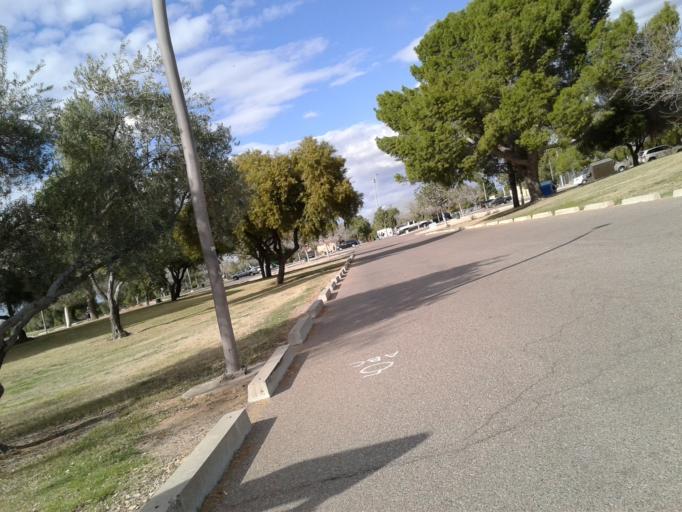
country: US
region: Arizona
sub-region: Maricopa County
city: Paradise Valley
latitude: 33.6045
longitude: -111.9579
